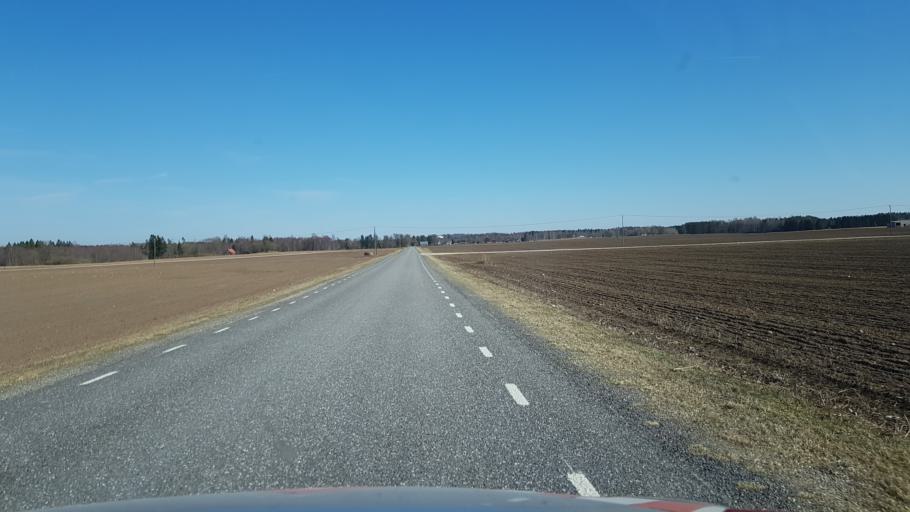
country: EE
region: Laeaene-Virumaa
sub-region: Rakke vald
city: Rakke
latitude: 59.0055
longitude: 26.1830
